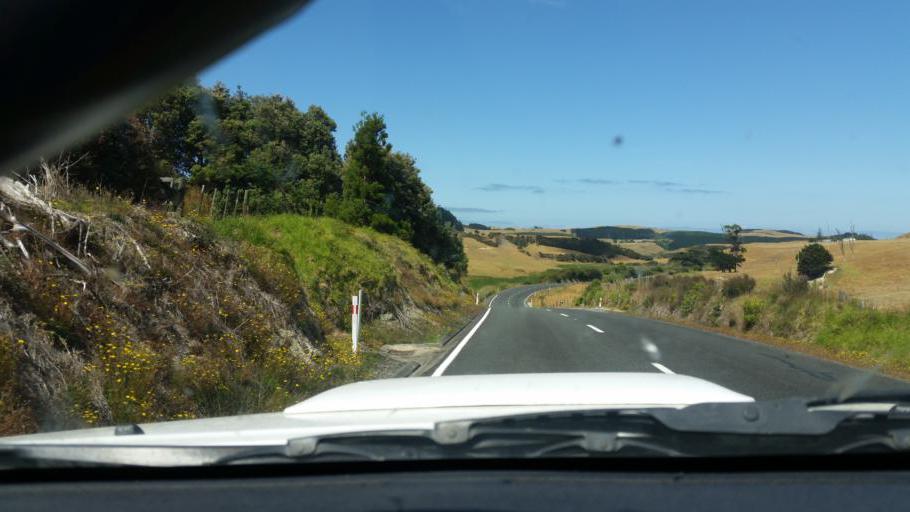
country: NZ
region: Northland
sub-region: Kaipara District
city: Dargaville
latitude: -35.8235
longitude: 173.6803
